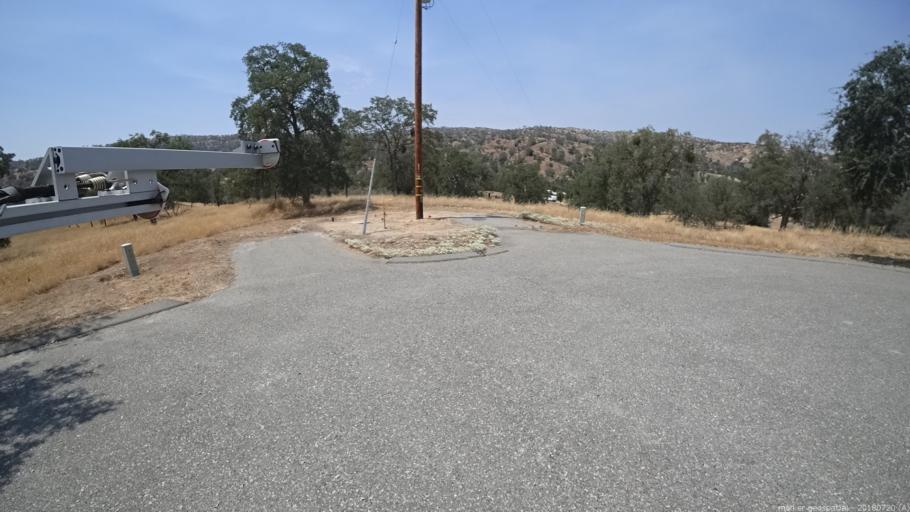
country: US
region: California
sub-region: Madera County
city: Yosemite Lakes
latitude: 37.1908
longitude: -119.8150
